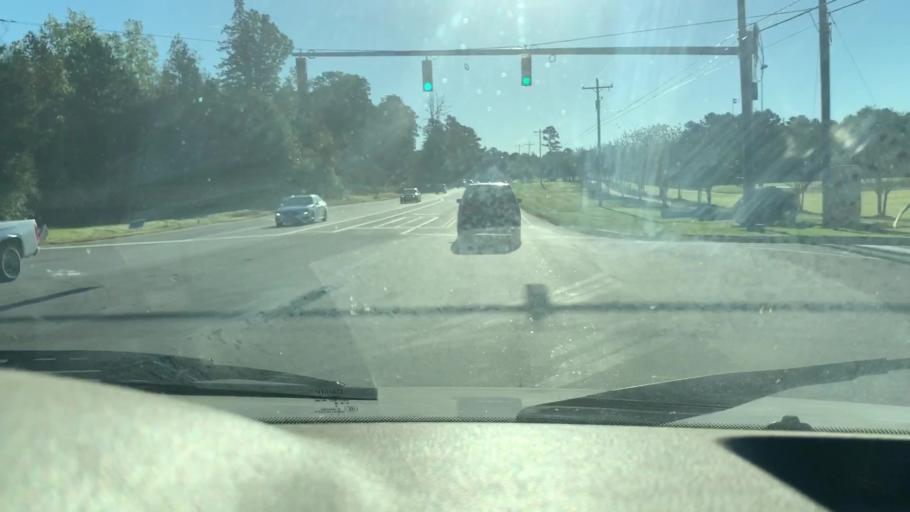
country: US
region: North Carolina
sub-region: Mecklenburg County
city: Huntersville
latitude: 35.4482
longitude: -80.7899
